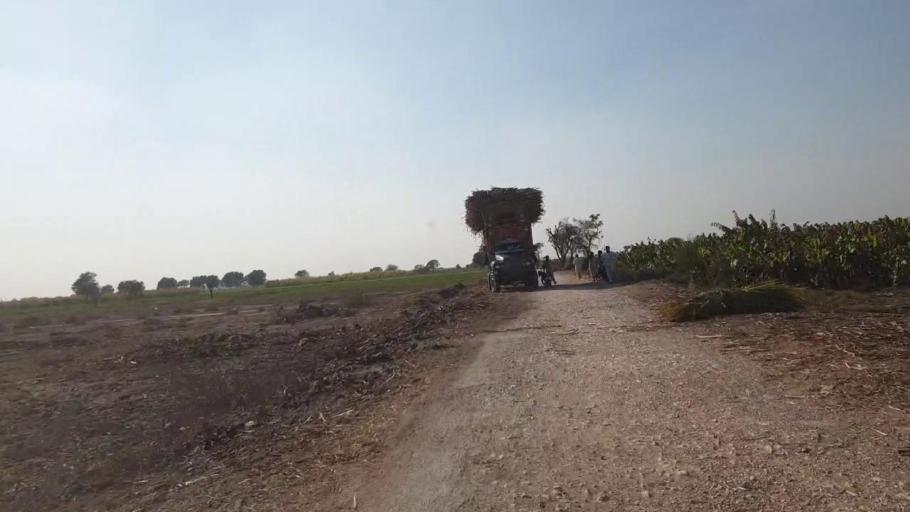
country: PK
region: Sindh
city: Chambar
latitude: 25.3175
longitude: 68.7625
